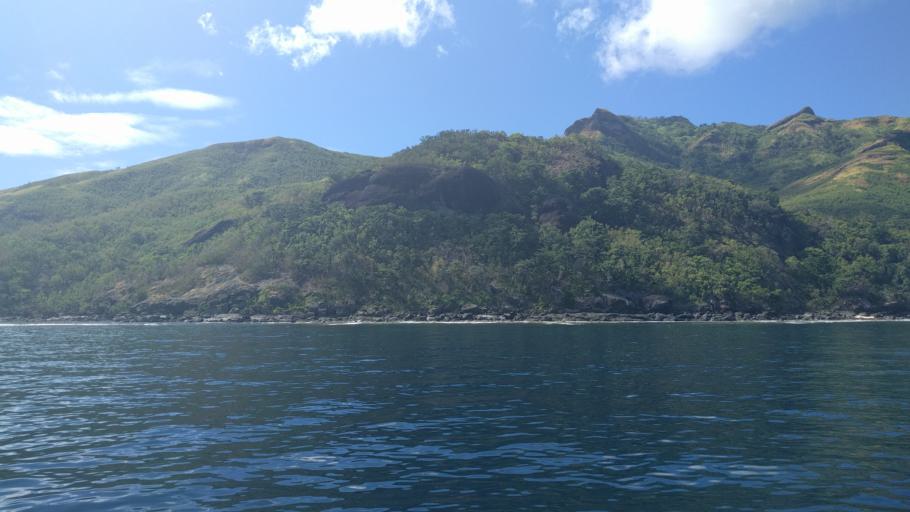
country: FJ
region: Western
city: Lautoka
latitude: -17.2891
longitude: 177.1008
